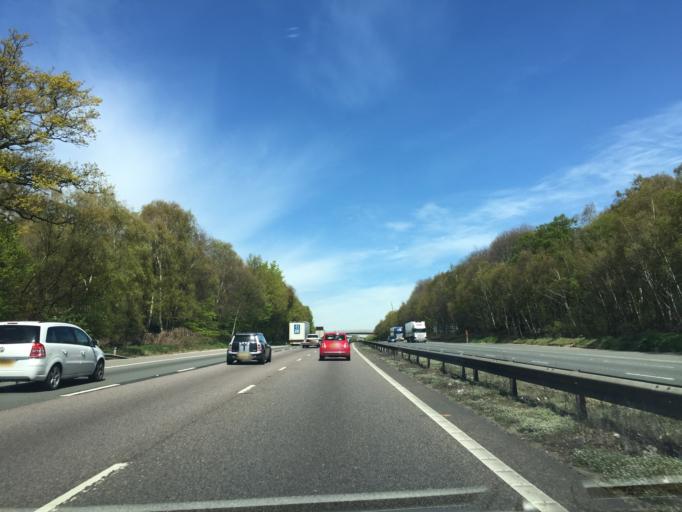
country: GB
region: England
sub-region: Essex
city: Epping
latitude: 51.6999
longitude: 0.1419
